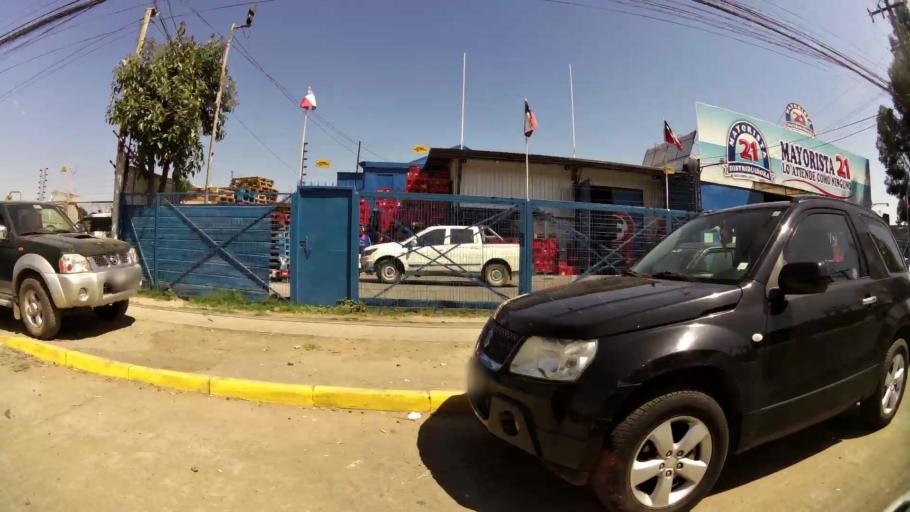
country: CL
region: Maule
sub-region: Provincia de Talca
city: Talca
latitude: -35.4225
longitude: -71.6368
